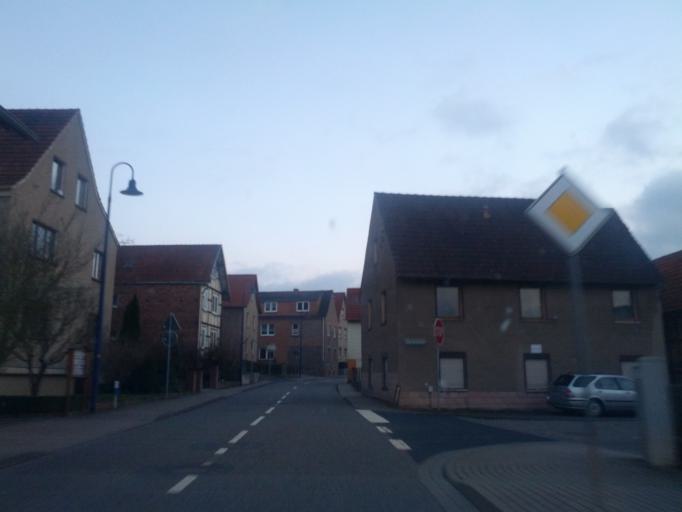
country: DE
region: Thuringia
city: Treffurt
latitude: 51.1054
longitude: 10.2213
